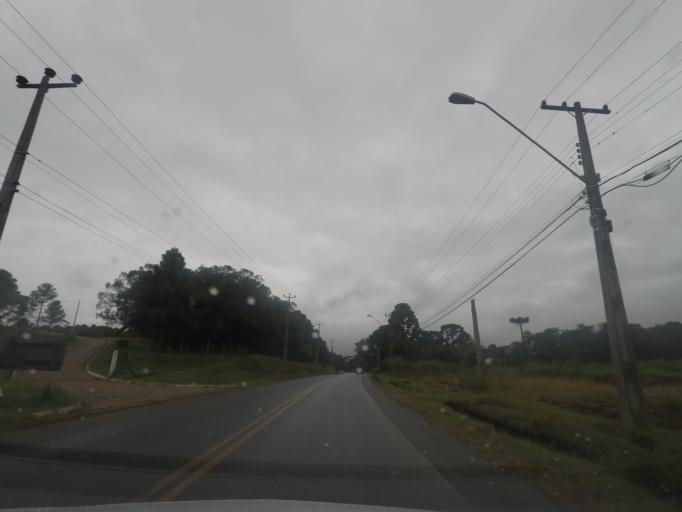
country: BR
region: Parana
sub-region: Campina Grande Do Sul
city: Campina Grande do Sul
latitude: -25.3213
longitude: -49.0768
